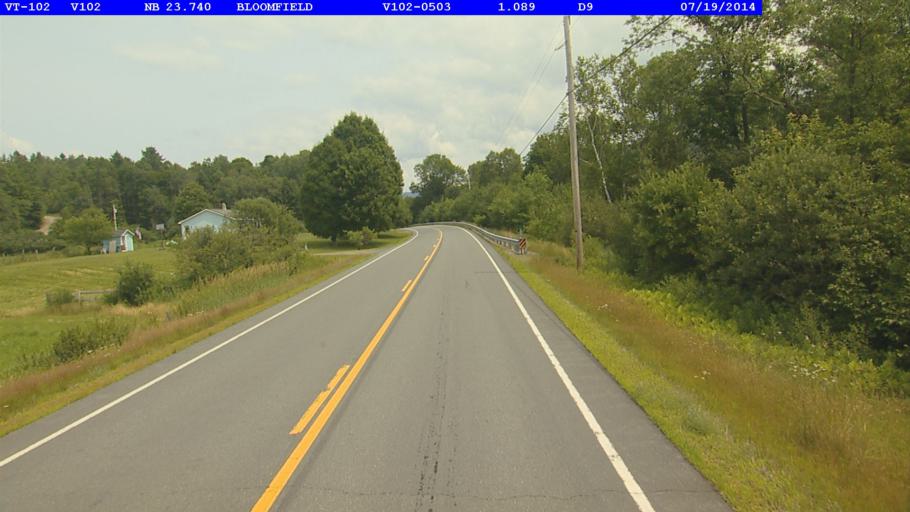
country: US
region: New Hampshire
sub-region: Coos County
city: Stratford
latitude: 44.7589
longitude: -71.6187
